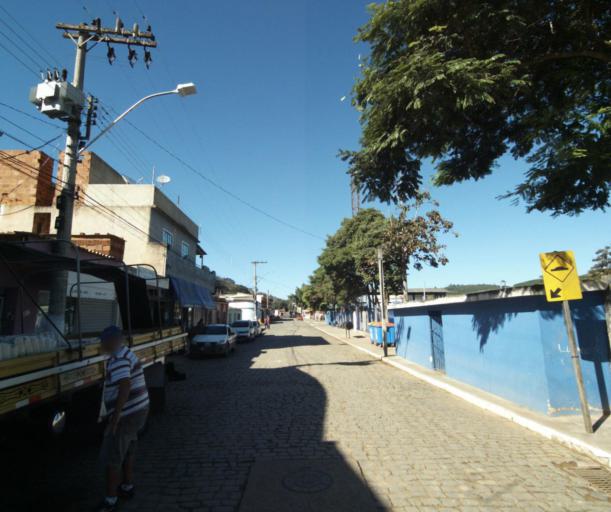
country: BR
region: Minas Gerais
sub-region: Espera Feliz
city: Espera Feliz
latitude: -20.6881
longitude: -41.8474
